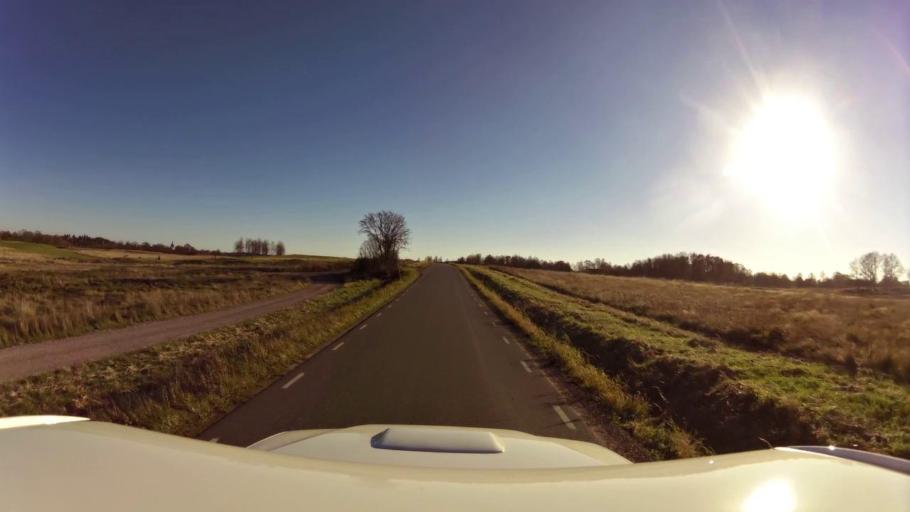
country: SE
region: OEstergoetland
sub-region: Kinda Kommun
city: Rimforsa
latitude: 58.2419
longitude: 15.6716
